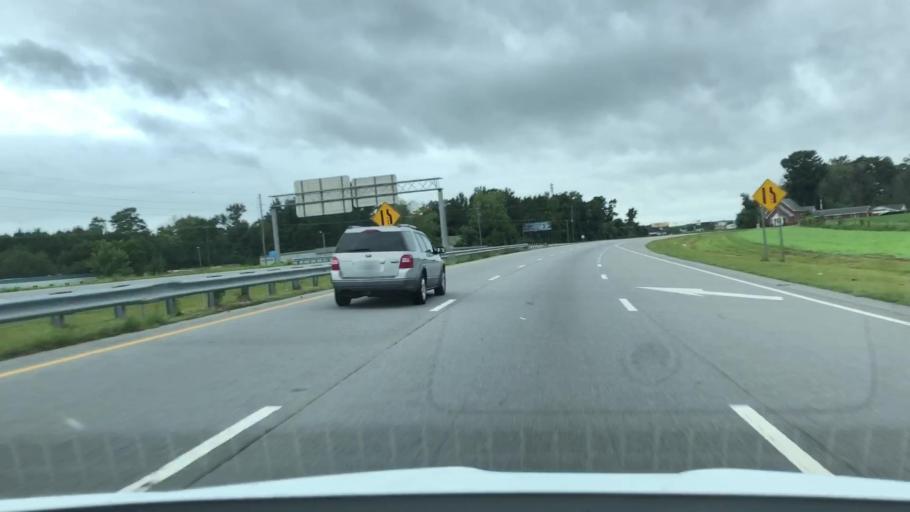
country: US
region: North Carolina
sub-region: Lenoir County
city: Kinston
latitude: 35.2622
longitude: -77.6879
